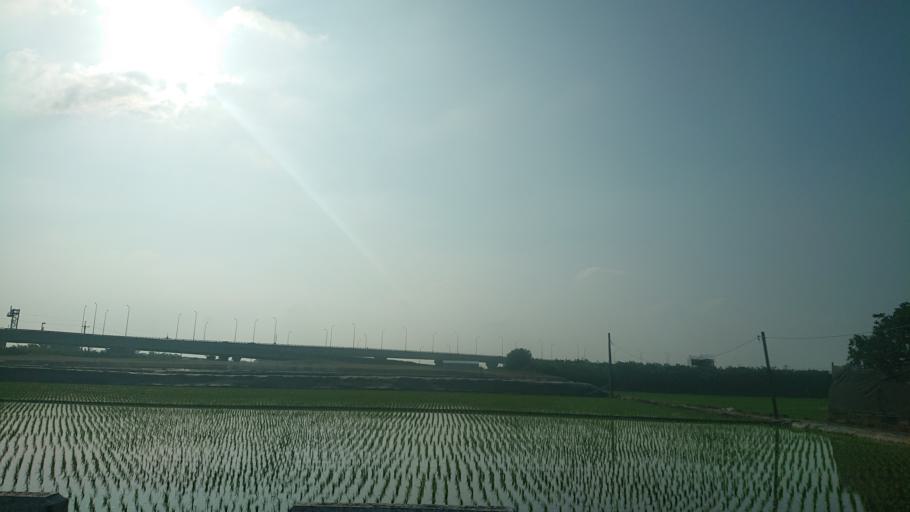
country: TW
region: Taiwan
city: Xinying
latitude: 23.1969
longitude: 120.2717
